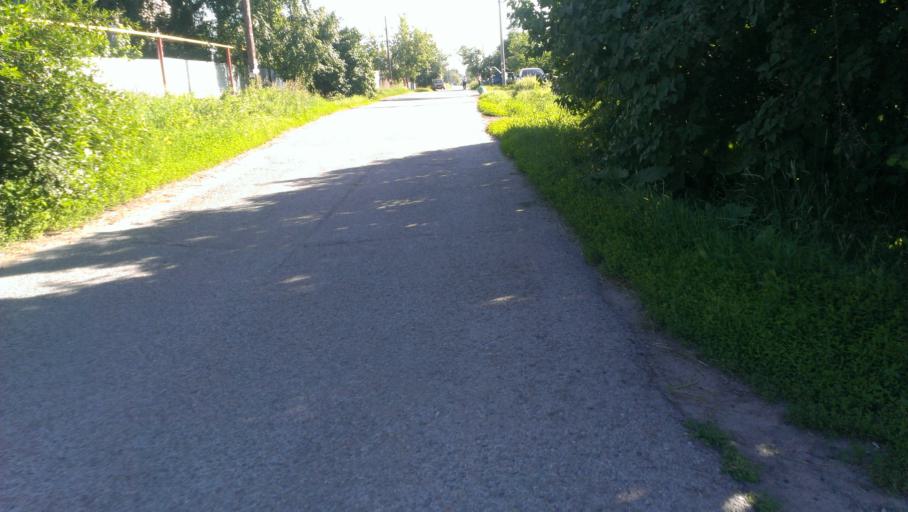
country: RU
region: Altai Krai
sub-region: Gorod Barnaulskiy
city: Barnaul
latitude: 53.3556
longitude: 83.7399
